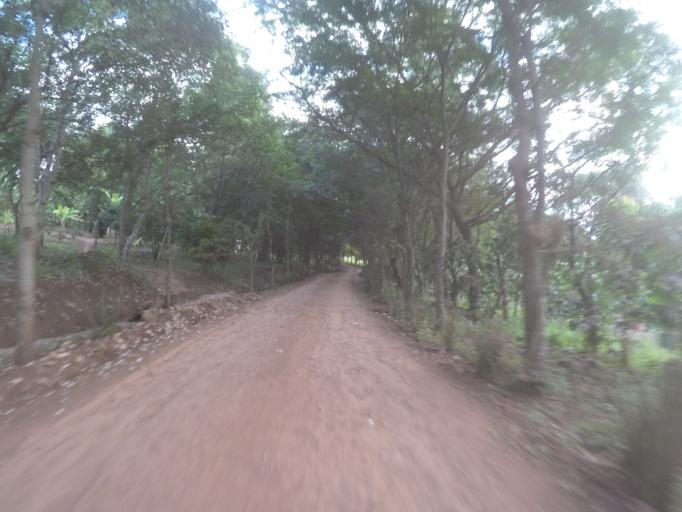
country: TZ
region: Arusha
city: Kiratu
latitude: -3.3210
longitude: 35.6623
